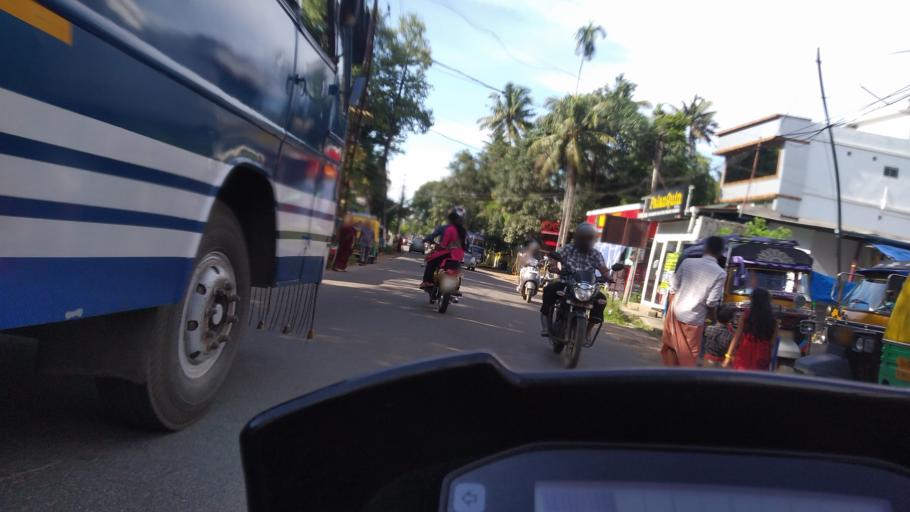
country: IN
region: Kerala
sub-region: Ernakulam
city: Elur
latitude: 10.0419
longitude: 76.2188
